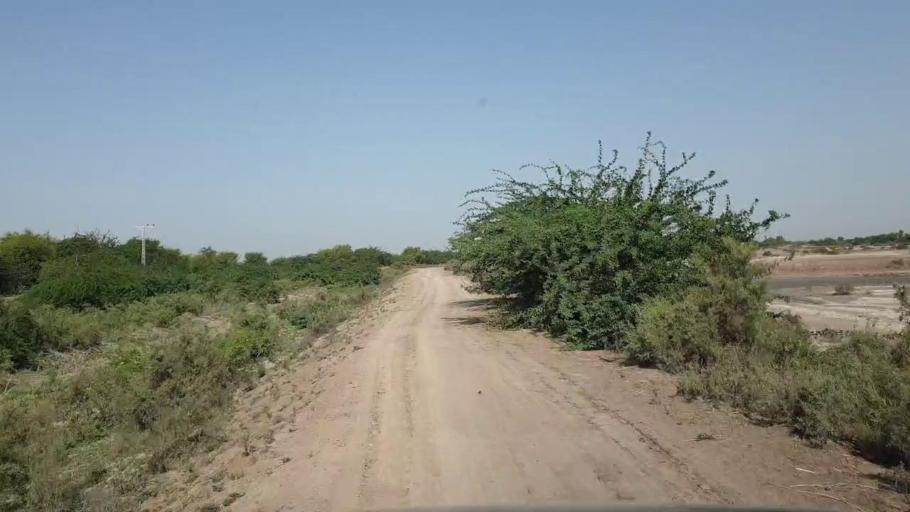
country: PK
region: Sindh
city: Tando Bago
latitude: 24.6630
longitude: 69.0676
